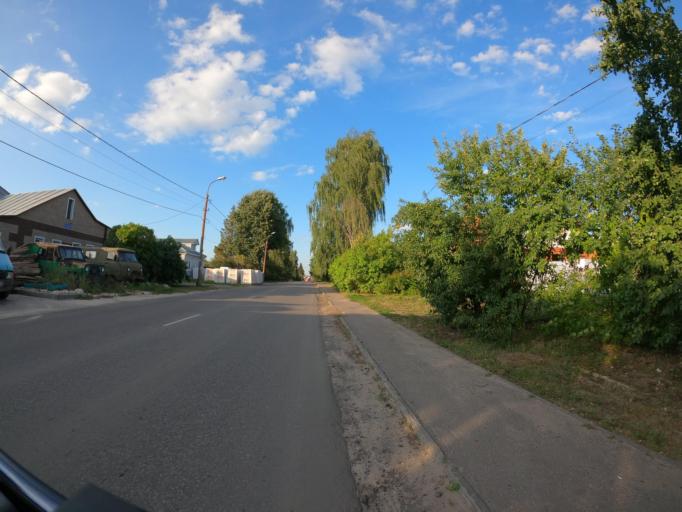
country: RU
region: Moskovskaya
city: Raduzhnyy
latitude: 55.1039
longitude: 38.7357
